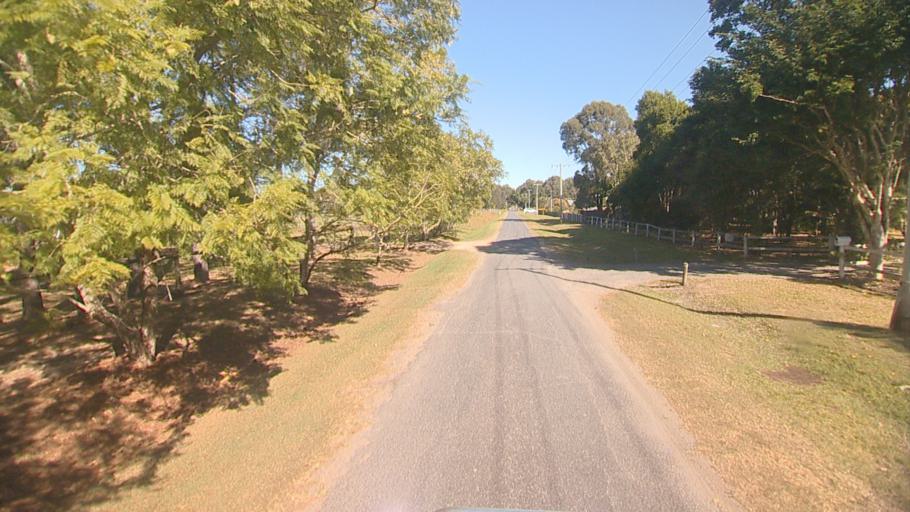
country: AU
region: Queensland
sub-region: Logan
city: Waterford West
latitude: -27.7161
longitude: 153.1266
